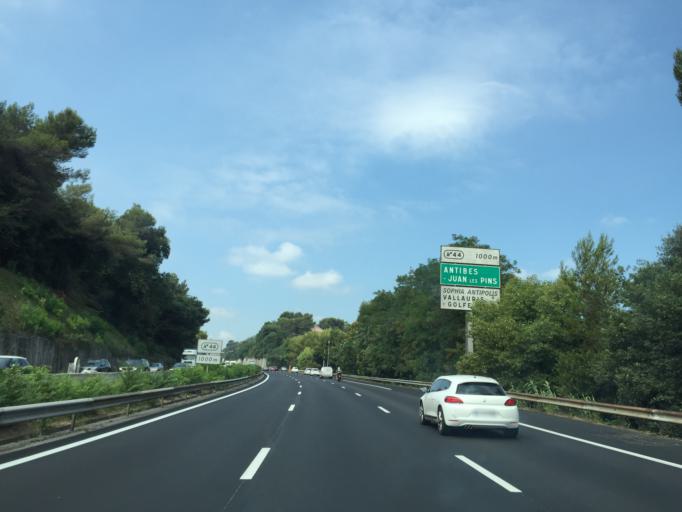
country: FR
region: Provence-Alpes-Cote d'Azur
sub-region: Departement des Alpes-Maritimes
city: Biot
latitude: 43.6104
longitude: 7.1019
